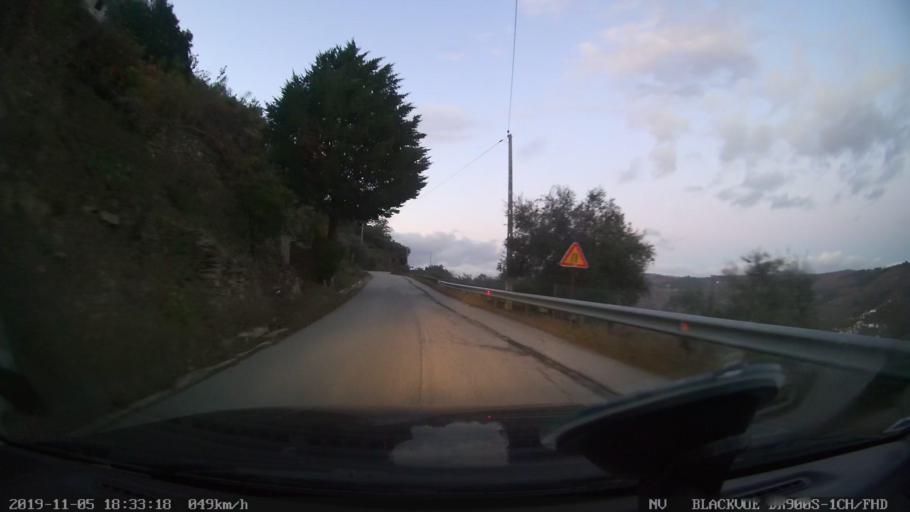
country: PT
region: Vila Real
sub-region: Sabrosa
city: Vilela
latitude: 41.2146
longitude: -7.5522
